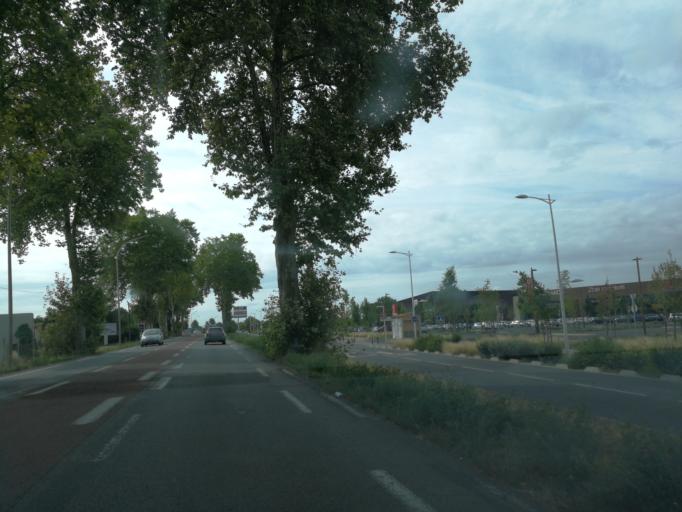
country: FR
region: Midi-Pyrenees
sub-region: Departement de la Haute-Garonne
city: Saint-Alban
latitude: 43.6924
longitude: 1.4024
